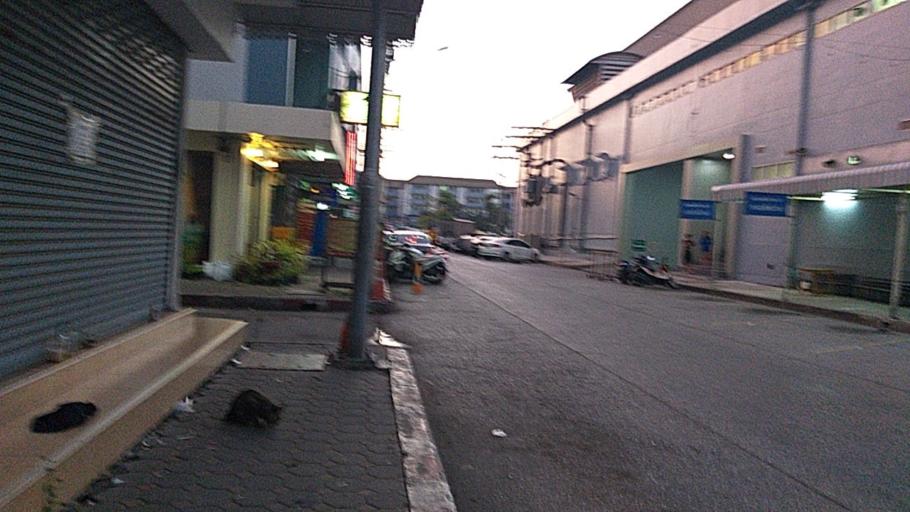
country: TH
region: Bangkok
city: Bang Na
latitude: 13.6678
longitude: 100.6830
